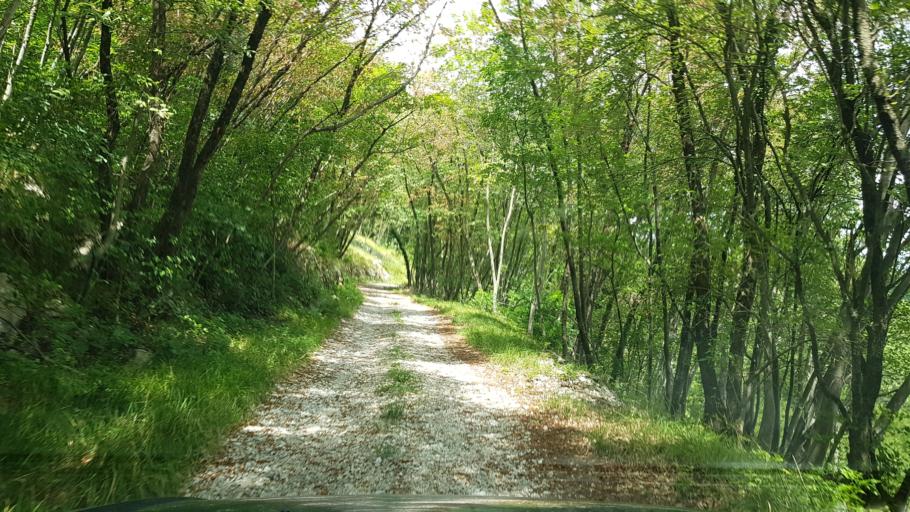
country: SI
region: Nova Gorica
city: Solkan
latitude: 46.0102
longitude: 13.6418
